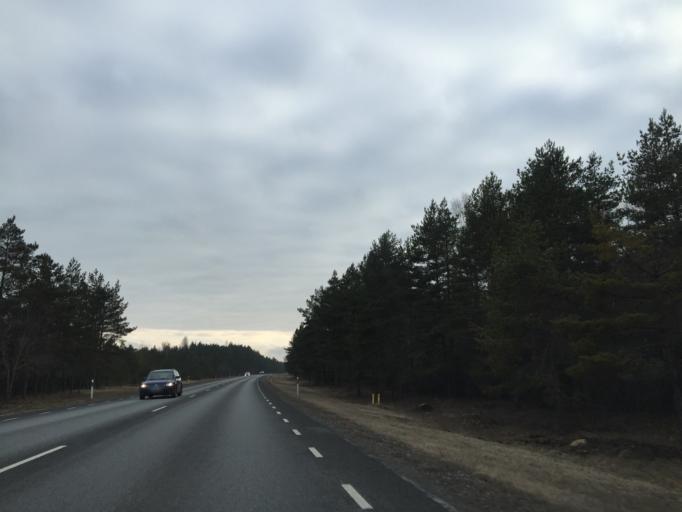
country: EE
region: Saare
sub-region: Orissaare vald
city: Orissaare
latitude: 58.4964
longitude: 22.8573
